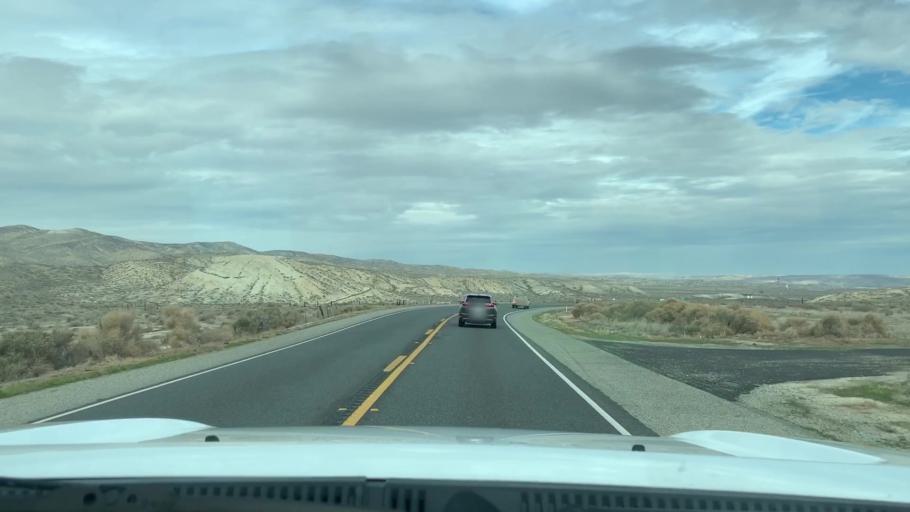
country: US
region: California
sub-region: Kern County
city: Maricopa
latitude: 35.0380
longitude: -119.4204
